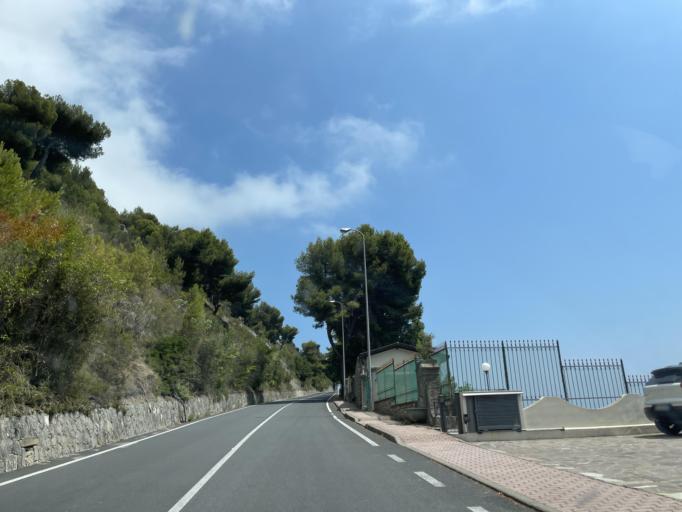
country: FR
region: Provence-Alpes-Cote d'Azur
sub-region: Departement des Alpes-Maritimes
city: Menton
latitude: 43.7864
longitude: 7.5439
